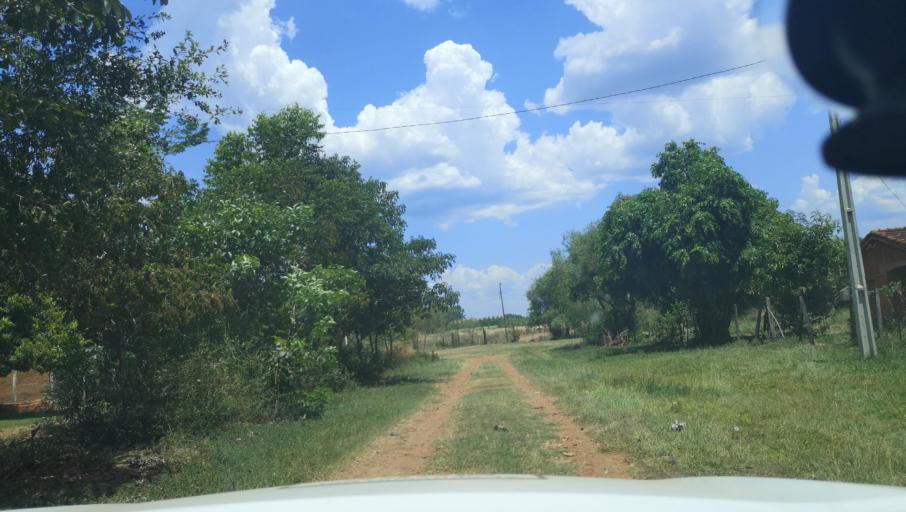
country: PY
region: Itapua
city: Carmen del Parana
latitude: -27.1715
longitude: -56.2414
